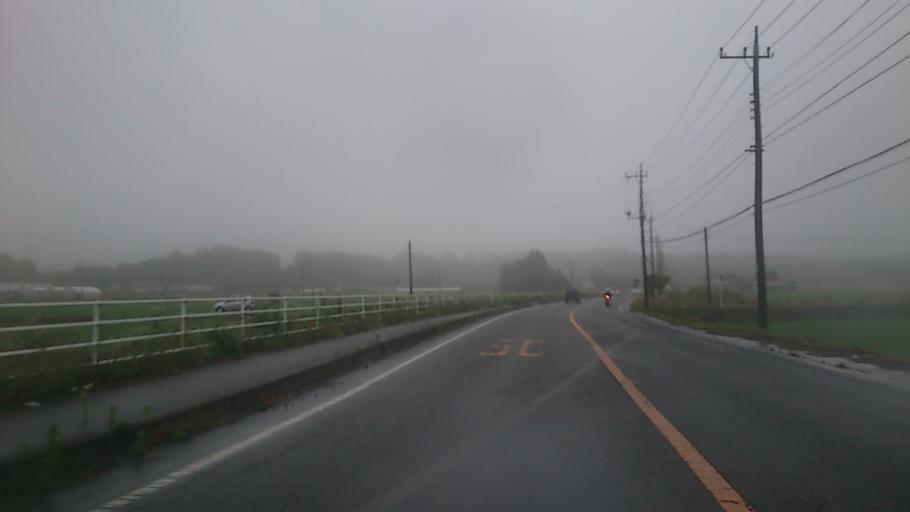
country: JP
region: Tochigi
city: Otawara
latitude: 36.8298
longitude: 140.0742
